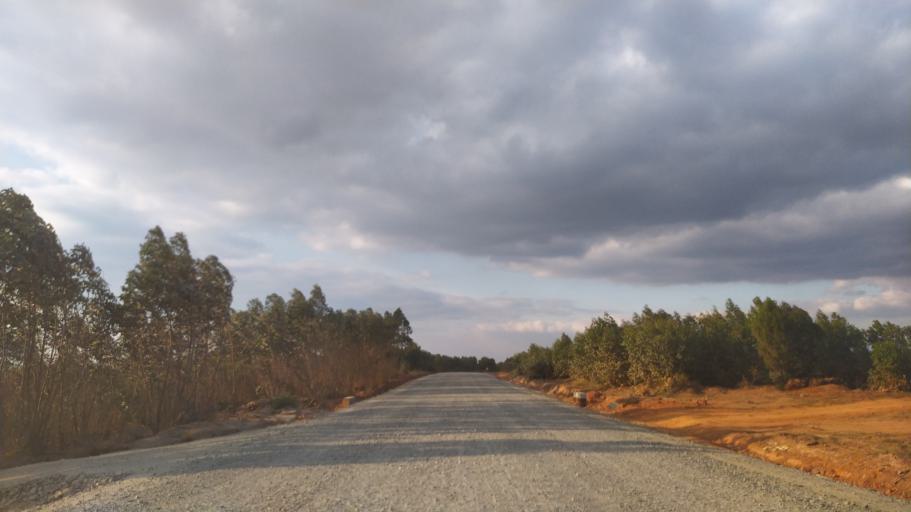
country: MG
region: Analamanga
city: Anjozorobe
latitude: -18.5207
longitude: 48.2624
